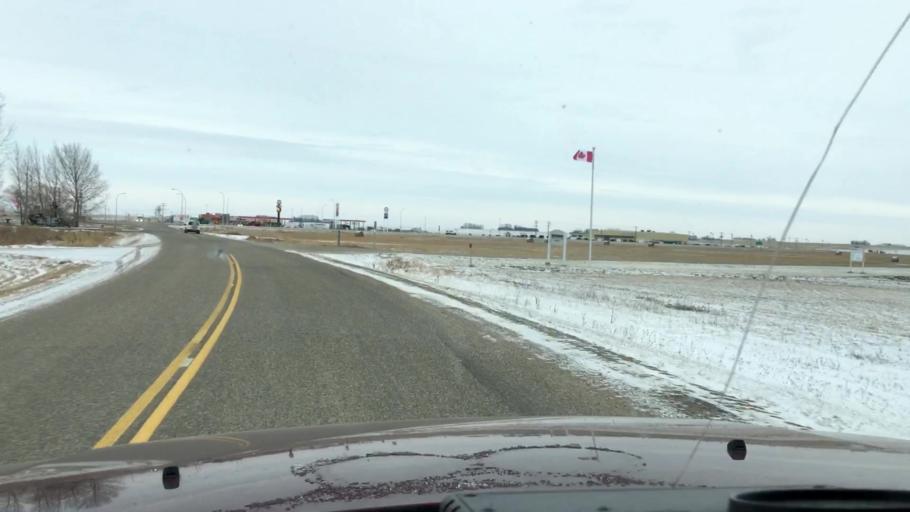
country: CA
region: Saskatchewan
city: Watrous
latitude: 51.2489
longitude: -105.9742
